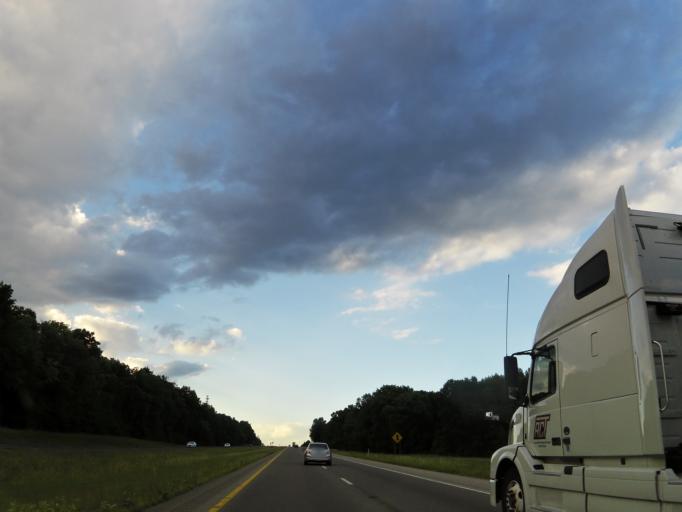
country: US
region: Tennessee
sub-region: Maury County
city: Spring Hill
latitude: 35.6792
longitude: -86.8884
